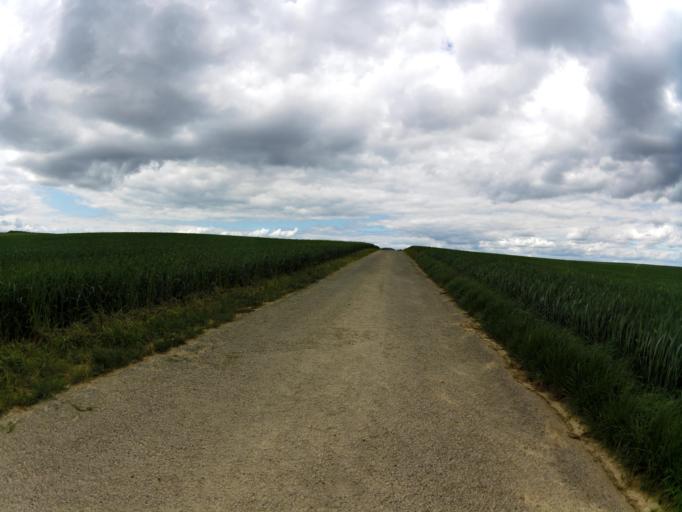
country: DE
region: Bavaria
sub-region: Regierungsbezirk Unterfranken
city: Gaukonigshofen
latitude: 49.6605
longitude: 10.0003
